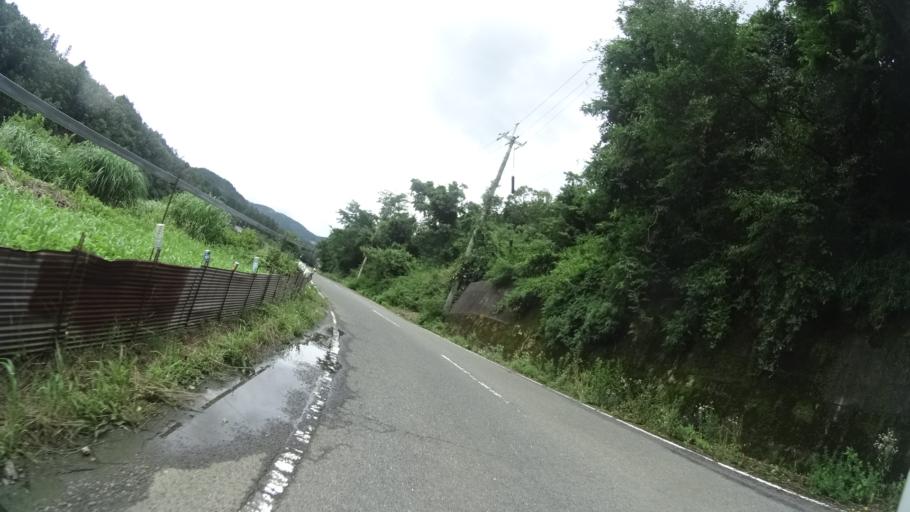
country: JP
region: Kyoto
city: Kameoka
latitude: 34.9555
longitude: 135.4978
